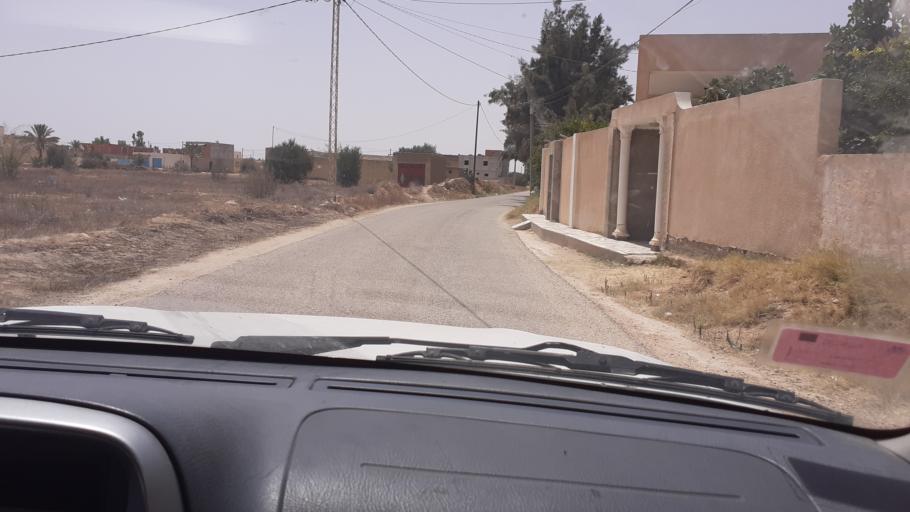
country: TN
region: Qabis
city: Matmata
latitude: 33.6107
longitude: 10.2874
